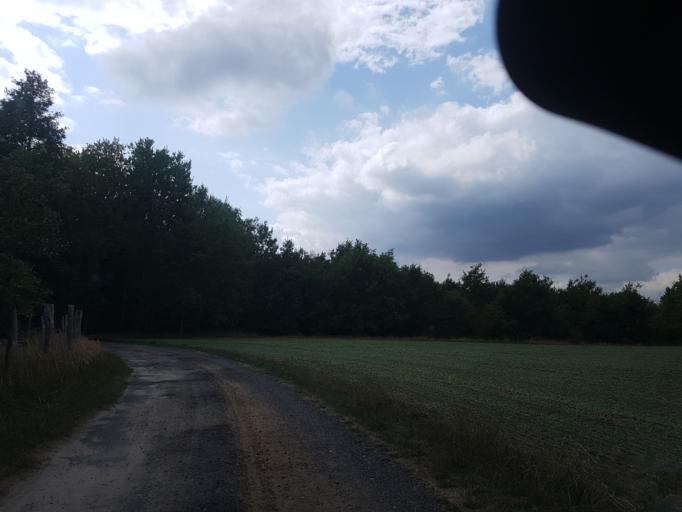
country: DE
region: Brandenburg
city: Treuenbrietzen
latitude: 52.0814
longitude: 12.8344
